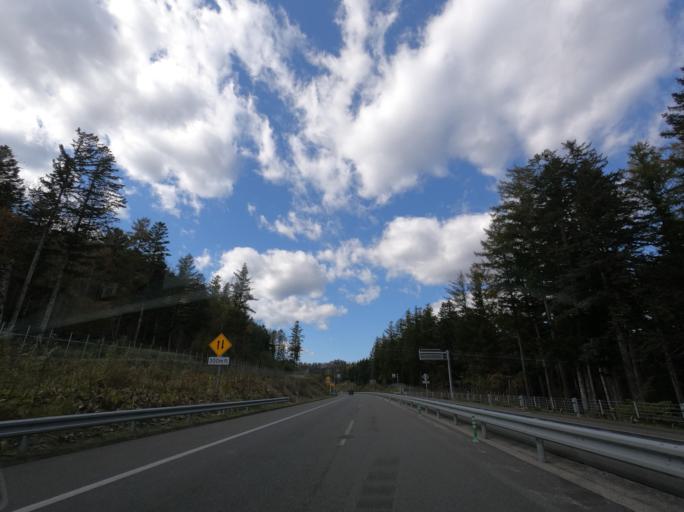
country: JP
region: Hokkaido
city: Kushiro
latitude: 43.0793
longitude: 144.0546
